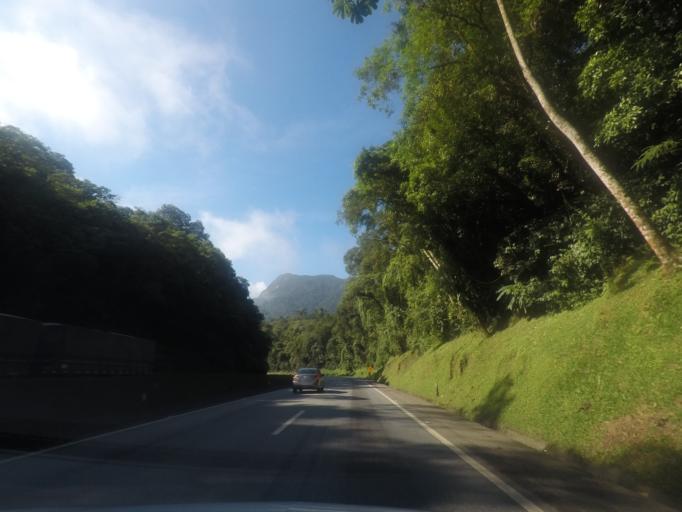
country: BR
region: Parana
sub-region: Piraquara
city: Piraquara
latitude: -25.5921
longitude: -48.8920
